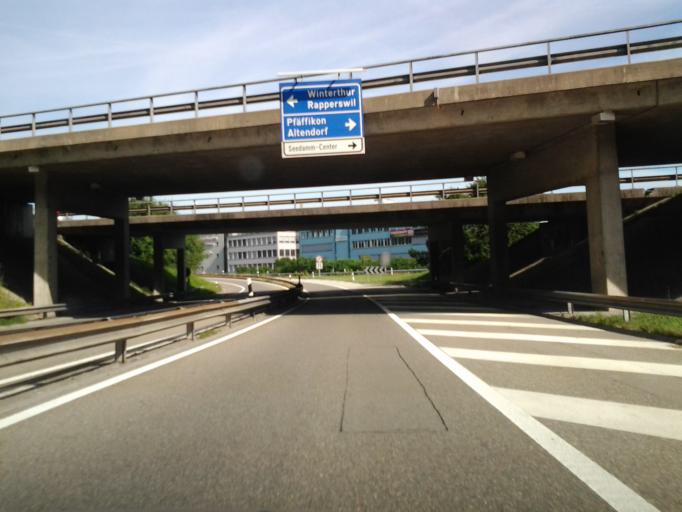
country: CH
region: Schwyz
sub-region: Bezirk March
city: Altendorf
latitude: 47.2003
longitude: 8.7994
